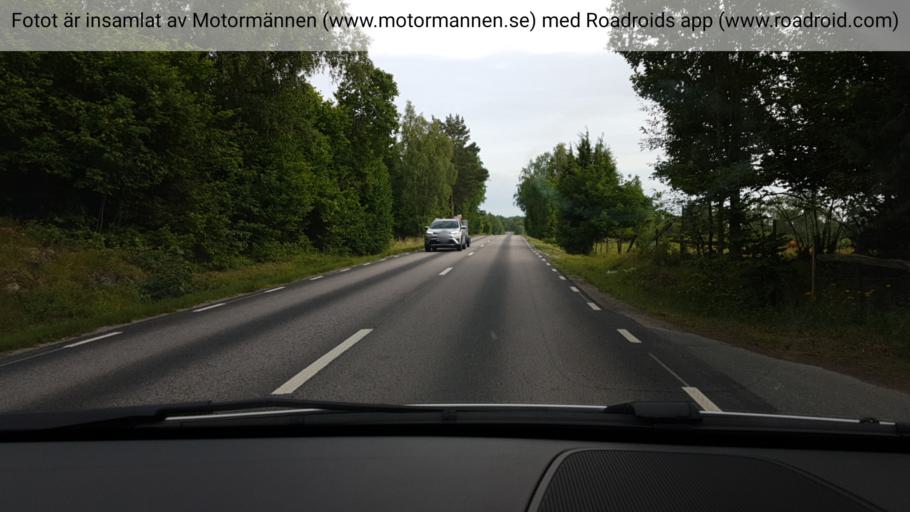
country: SE
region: Stockholm
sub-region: Norrtalje Kommun
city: Arno
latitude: 60.0332
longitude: 18.7831
